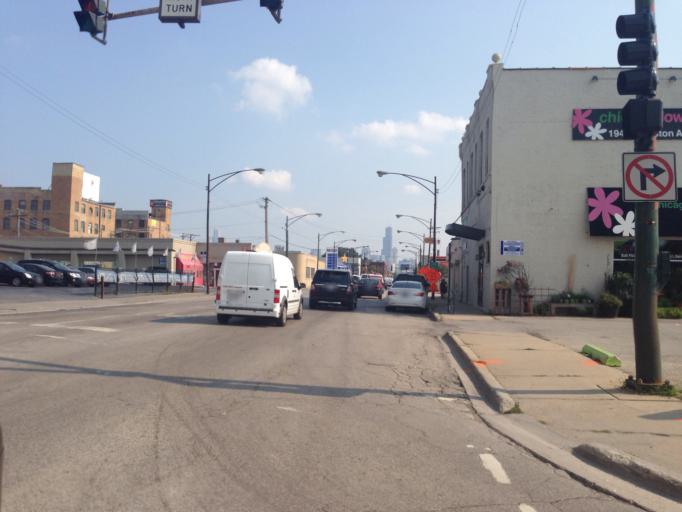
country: US
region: Illinois
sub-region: Cook County
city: Chicago
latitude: 41.9180
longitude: -87.6675
